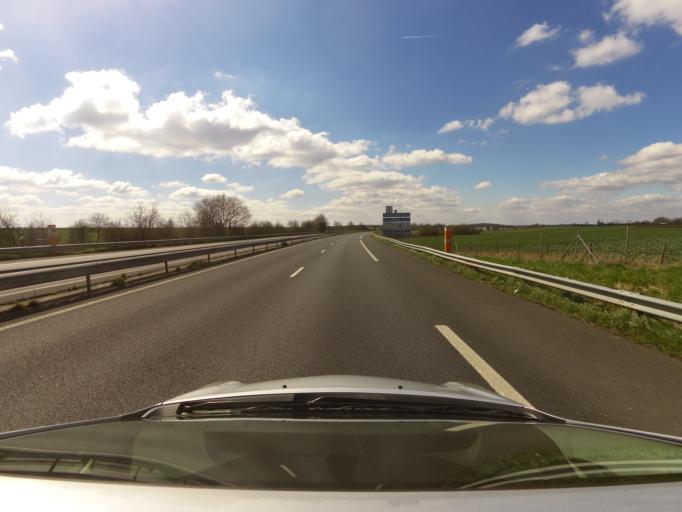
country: FR
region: Haute-Normandie
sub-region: Departement de la Seine-Maritime
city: Saint-Saens
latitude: 49.6827
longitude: 1.3473
